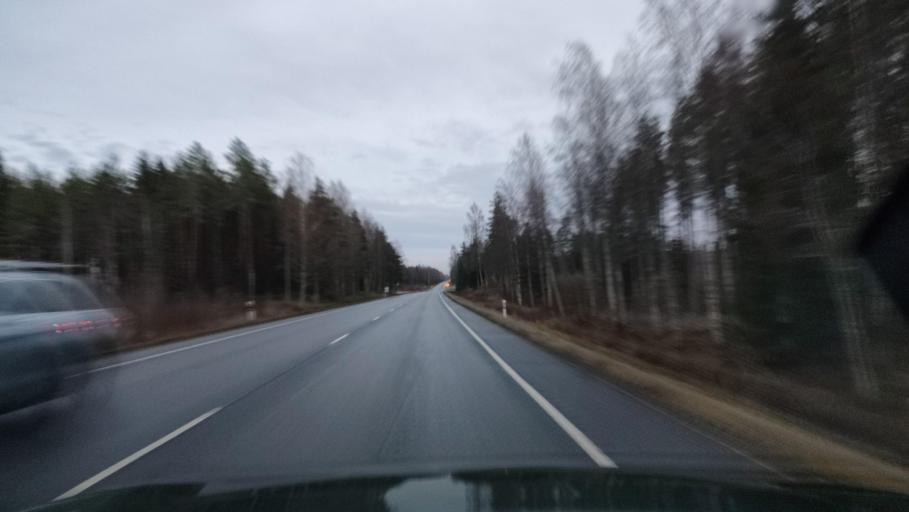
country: FI
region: Ostrobothnia
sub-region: Vaasa
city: Ristinummi
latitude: 63.0107
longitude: 21.7618
